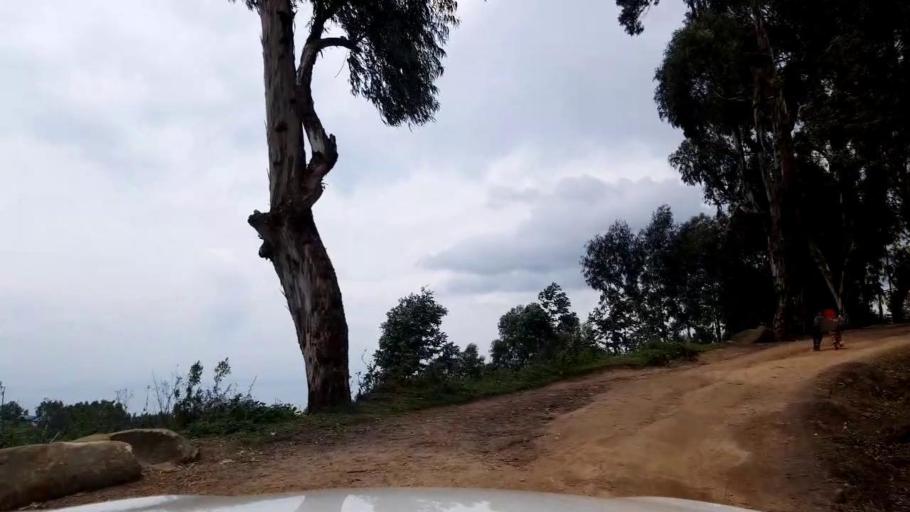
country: RW
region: Western Province
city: Kibuye
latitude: -1.9658
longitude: 29.3945
